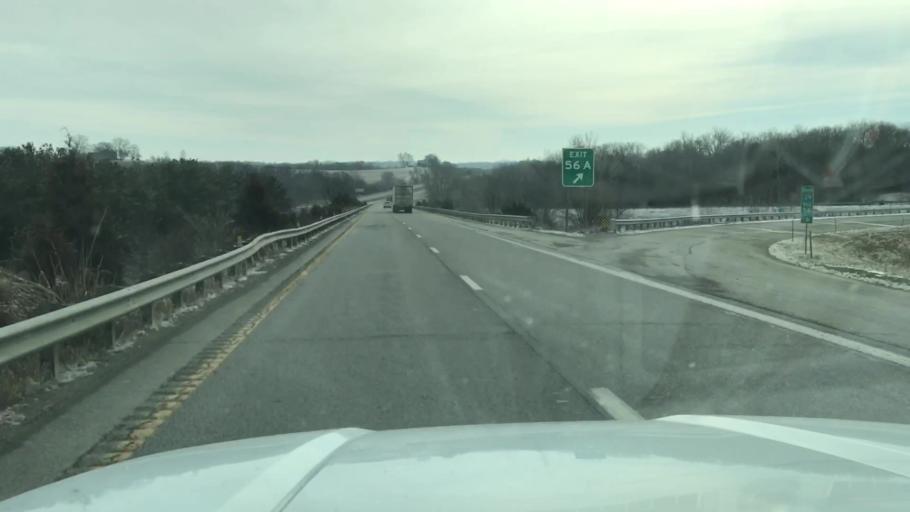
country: US
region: Missouri
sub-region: Andrew County
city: Country Club Village
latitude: 39.8834
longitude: -94.8539
